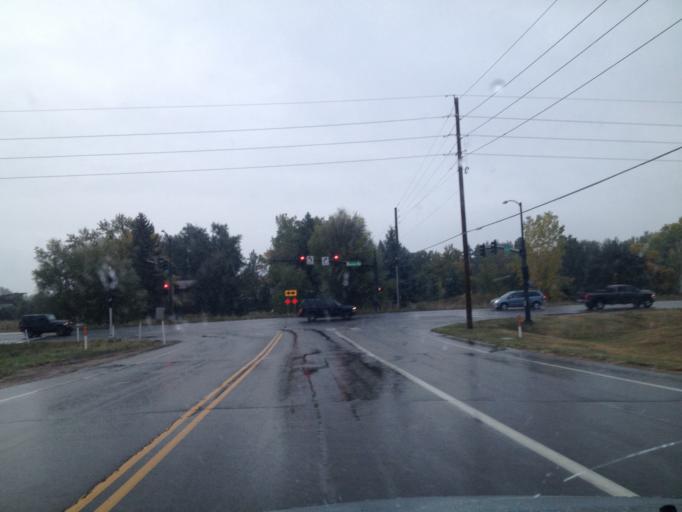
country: US
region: Colorado
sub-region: Boulder County
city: Superior
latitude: 39.9996
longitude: -105.1749
